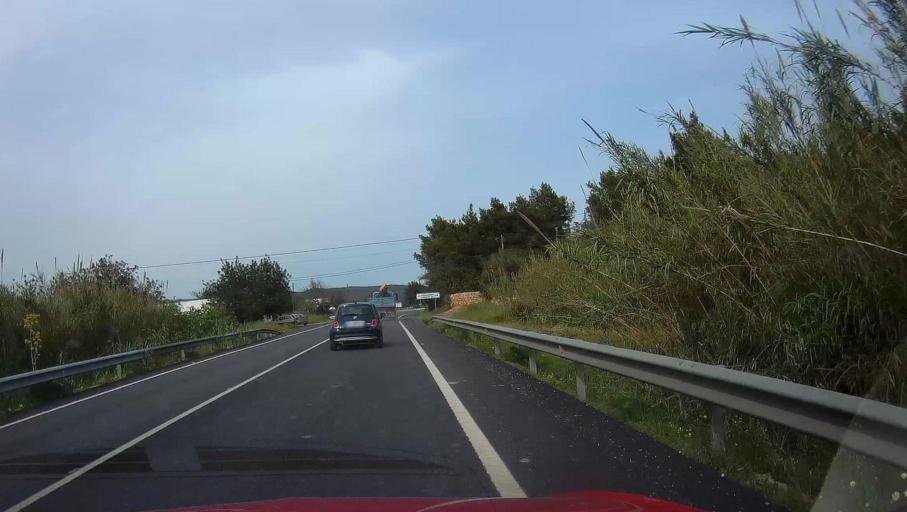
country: ES
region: Balearic Islands
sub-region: Illes Balears
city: Santa Eularia des Riu
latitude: 38.9811
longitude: 1.4829
